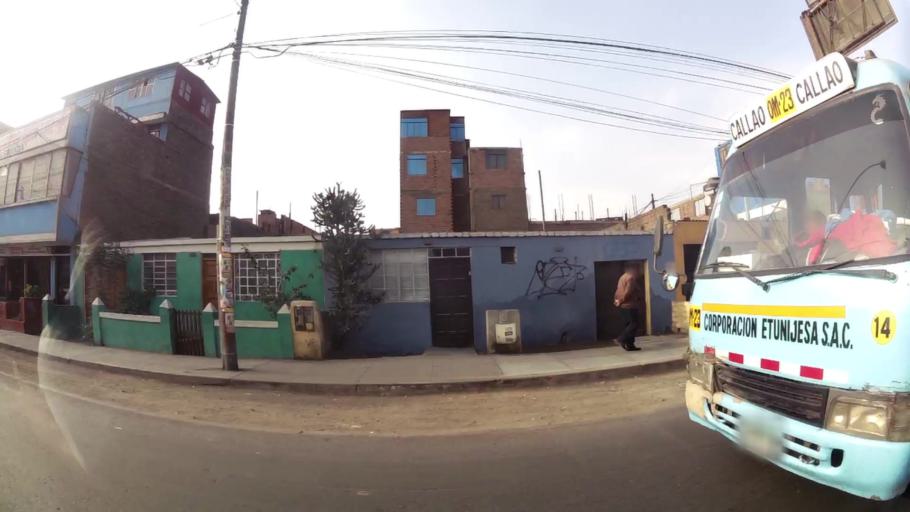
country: PE
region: Lima
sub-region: Lima
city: Independencia
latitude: -12.0255
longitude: -77.0769
